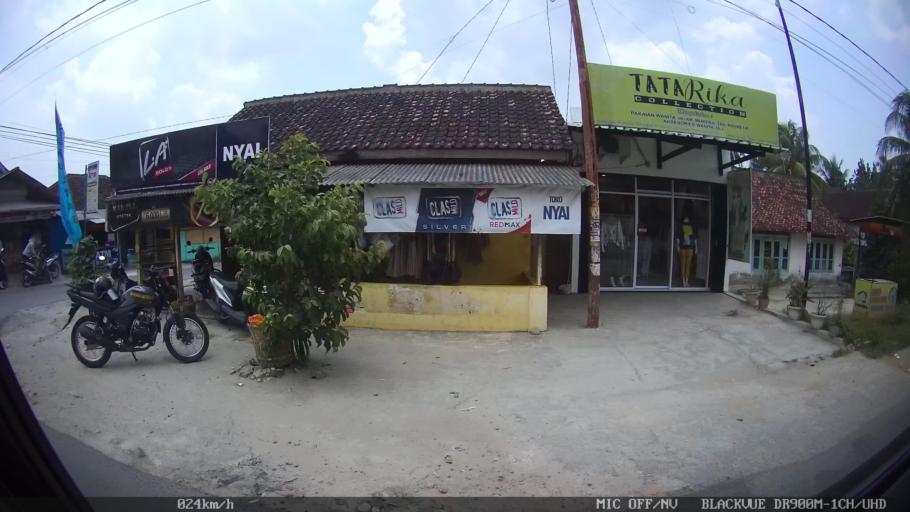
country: ID
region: Lampung
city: Pringsewu
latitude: -5.3501
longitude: 104.9731
